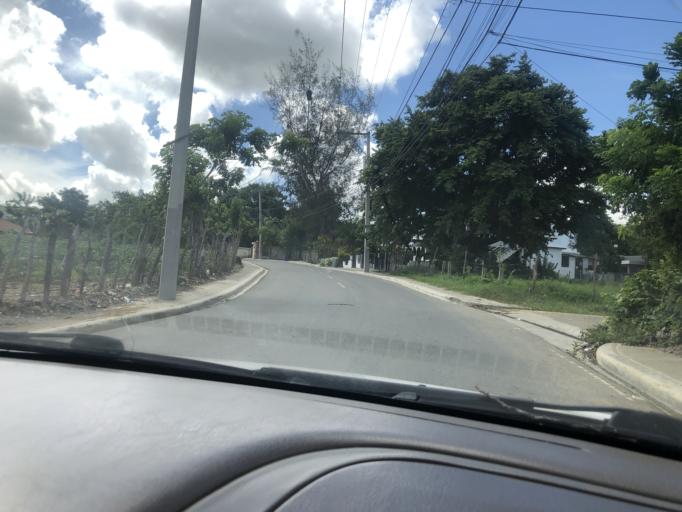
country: DO
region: Santiago
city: Santiago de los Caballeros
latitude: 19.4109
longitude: -70.7093
